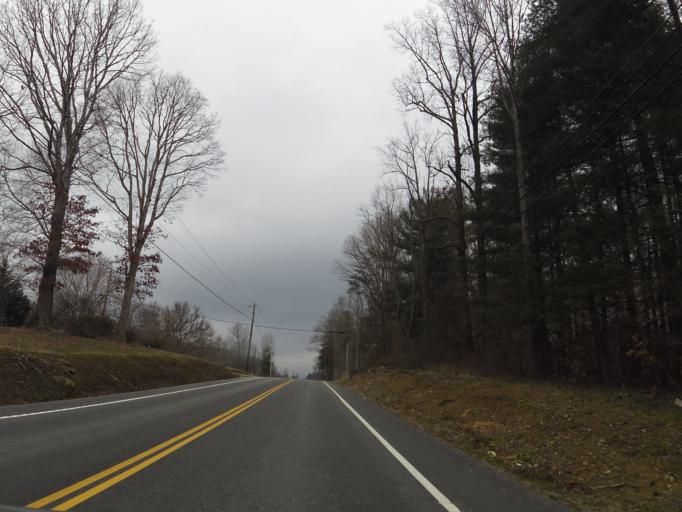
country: US
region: Tennessee
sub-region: Morgan County
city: Wartburg
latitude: 36.0615
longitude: -84.5352
